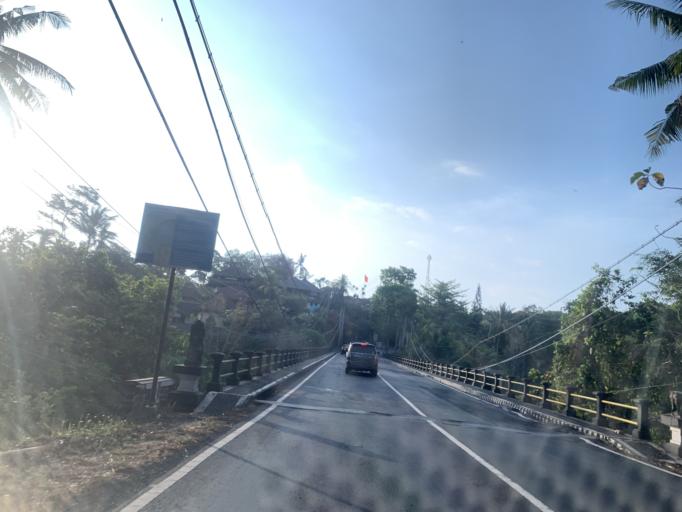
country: ID
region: Bali
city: Banjar Delodrurung
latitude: -8.4993
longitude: 114.9682
